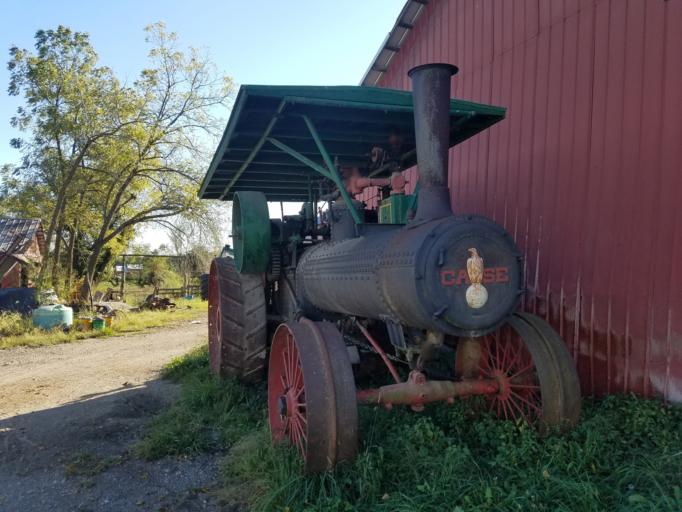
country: US
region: Iowa
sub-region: Decatur County
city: Lamoni
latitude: 40.6213
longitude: -93.8442
